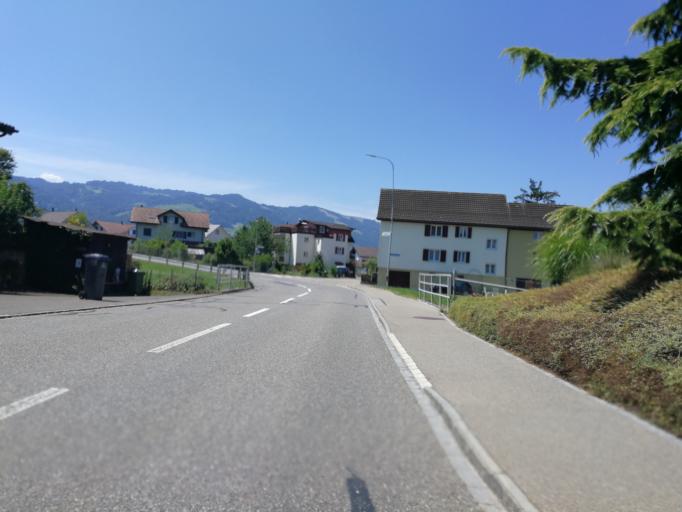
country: CH
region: Schwyz
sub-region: Bezirk March
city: Lachen
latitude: 47.1992
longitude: 8.8835
